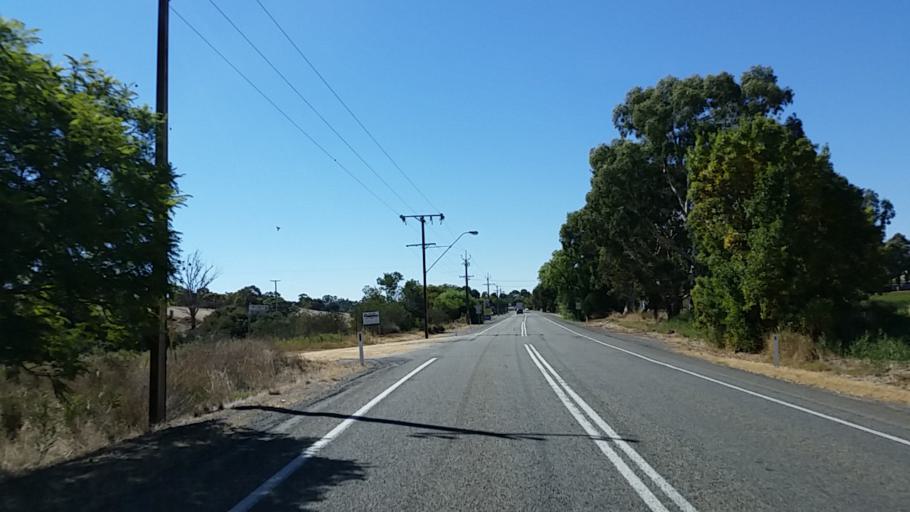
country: AU
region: South Australia
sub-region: Light
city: Kapunda
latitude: -34.0879
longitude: 138.7761
